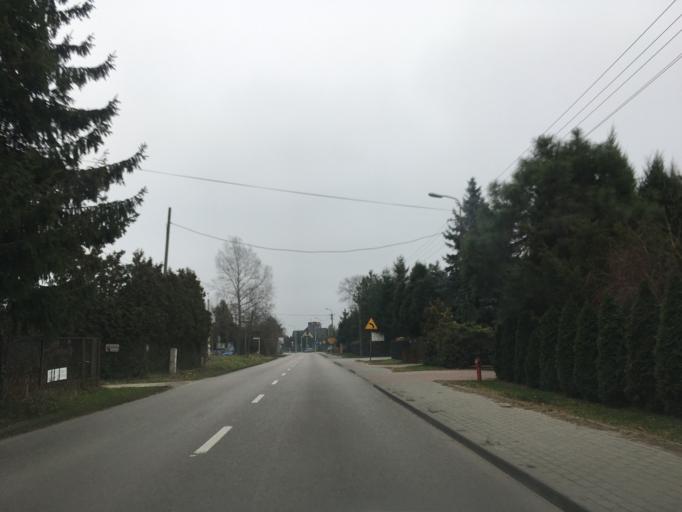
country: PL
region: Masovian Voivodeship
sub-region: Powiat piaseczynski
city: Lesznowola
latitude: 52.0506
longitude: 20.9301
